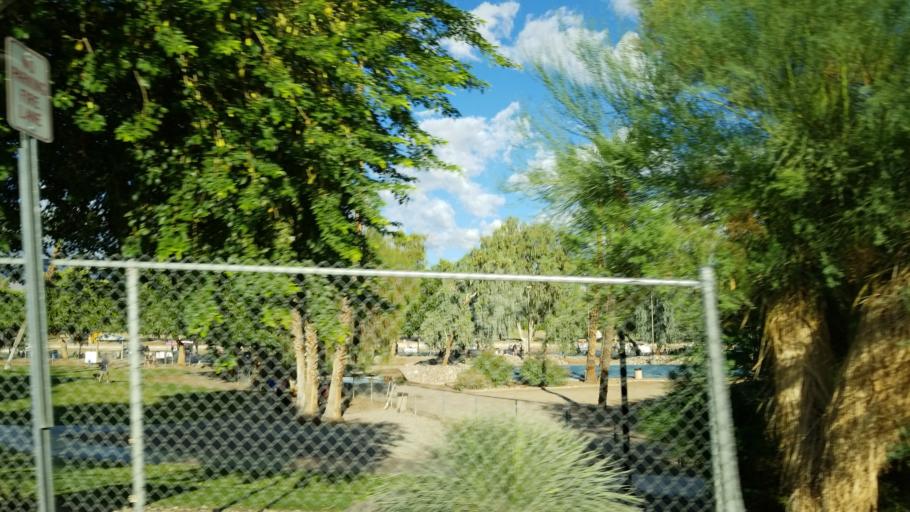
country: US
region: Arizona
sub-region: Mohave County
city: Lake Havasu City
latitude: 34.4671
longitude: -114.3489
